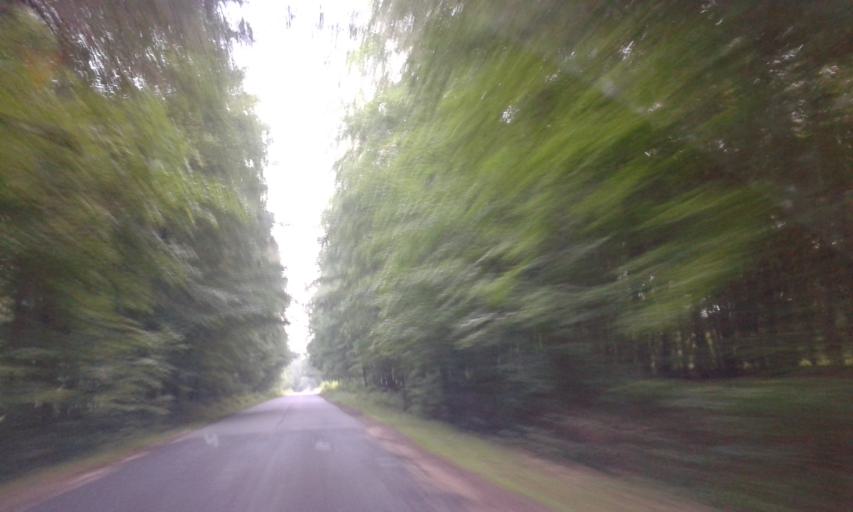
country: PL
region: Kujawsko-Pomorskie
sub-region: Powiat sepolenski
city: Sypniewo
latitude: 53.4516
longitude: 17.3634
